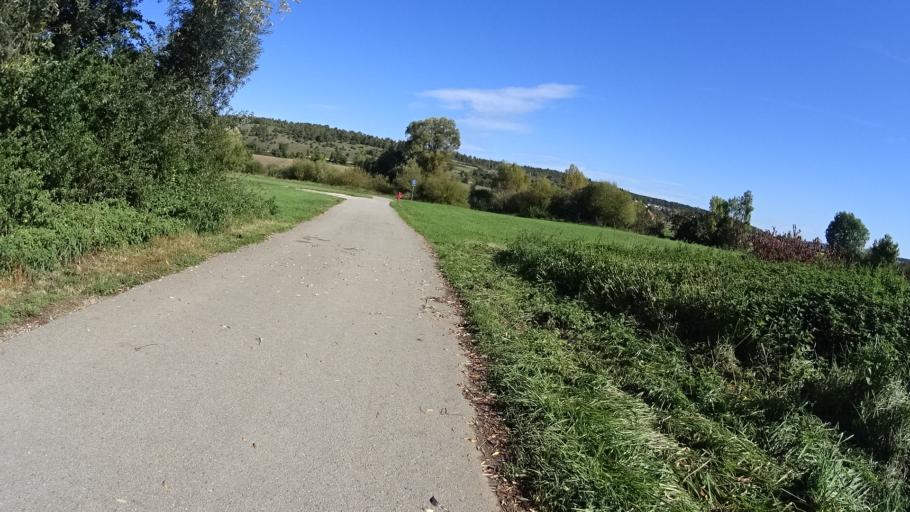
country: DE
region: Bavaria
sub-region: Upper Bavaria
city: Eichstaett
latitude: 48.8756
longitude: 11.2192
